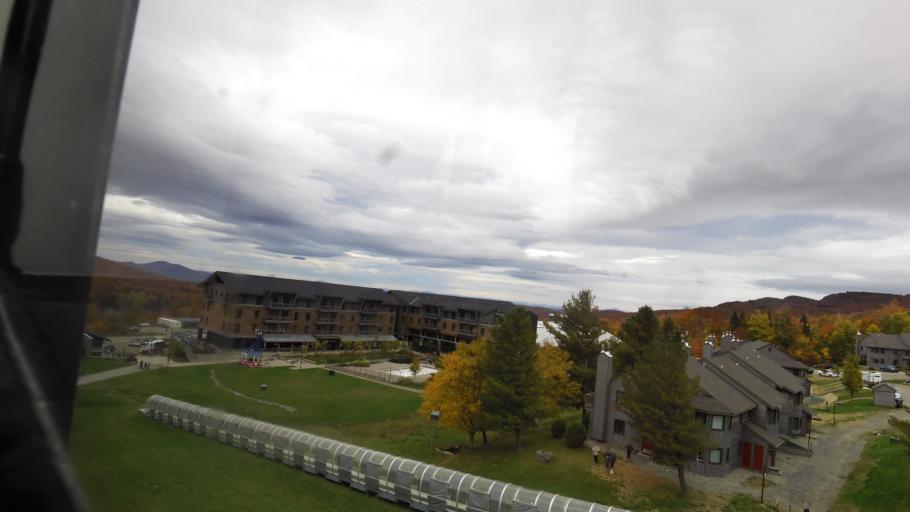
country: US
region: Vermont
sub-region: Franklin County
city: Richford
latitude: 44.9381
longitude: -72.5071
